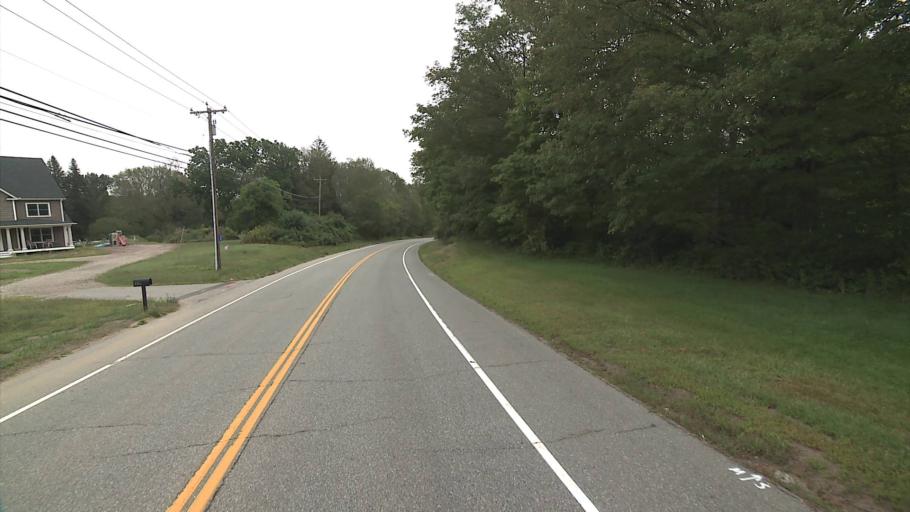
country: US
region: Connecticut
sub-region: Tolland County
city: Hebron
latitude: 41.6752
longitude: -72.4009
